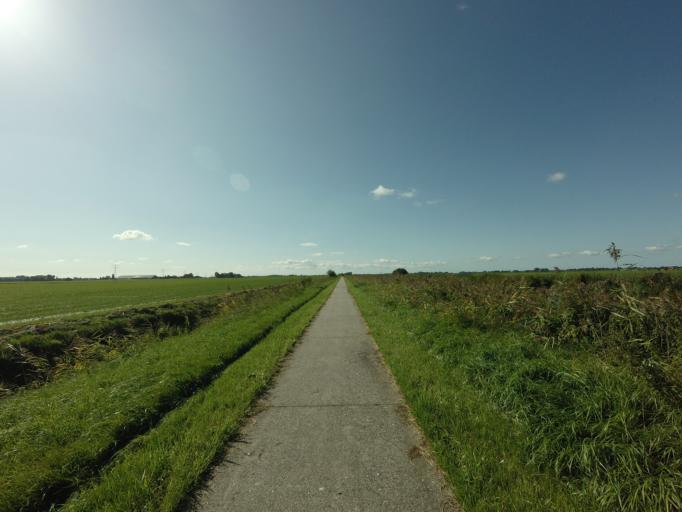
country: NL
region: Friesland
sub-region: Gemeente Boarnsterhim
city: Reduzum
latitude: 53.1416
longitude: 5.7636
